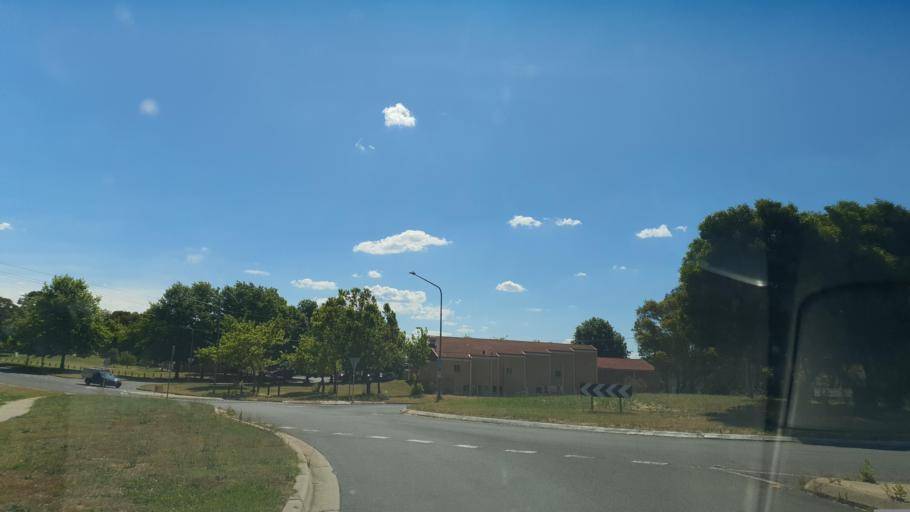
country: AU
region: Australian Capital Territory
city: Macquarie
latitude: -35.2262
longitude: 149.0563
